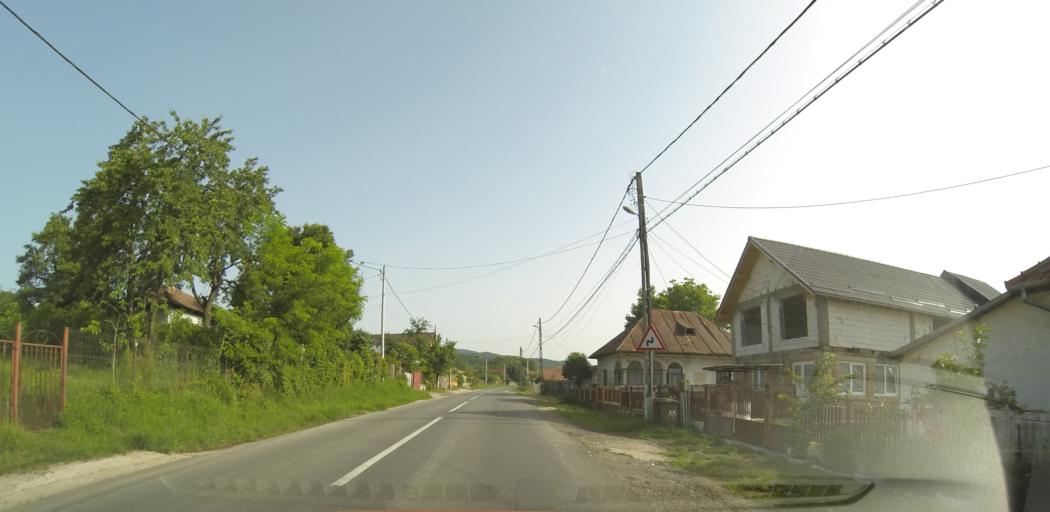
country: RO
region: Valcea
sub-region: Comuna Pausesti-Maglasi
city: Pausesti-Maglasi
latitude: 45.1481
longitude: 24.2456
